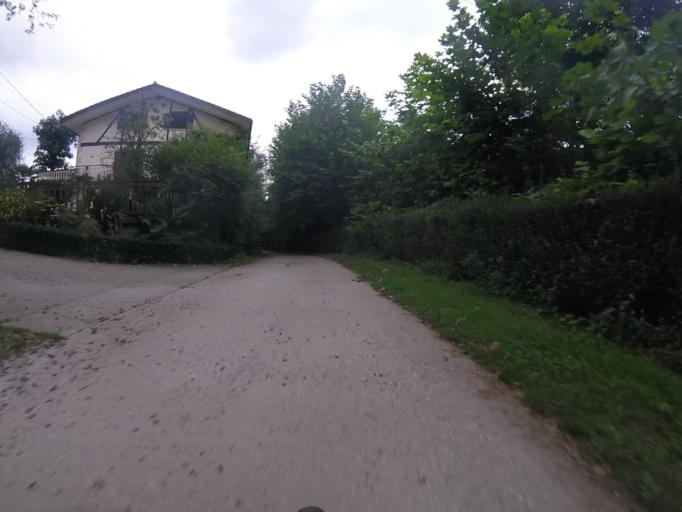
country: ES
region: Basque Country
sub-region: Provincia de Guipuzcoa
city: Errenteria
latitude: 43.2790
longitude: -1.8481
